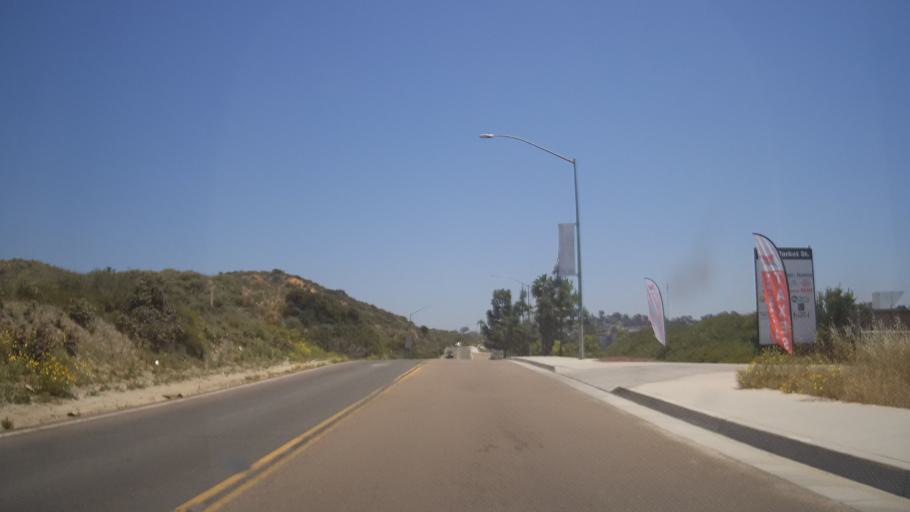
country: US
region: California
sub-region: San Diego County
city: National City
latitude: 32.7104
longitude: -117.0811
